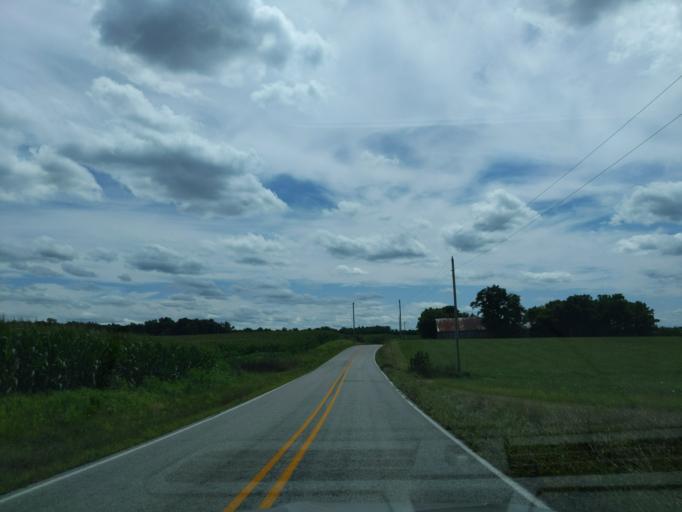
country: US
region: Indiana
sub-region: Ripley County
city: Osgood
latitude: 39.2124
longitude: -85.2750
